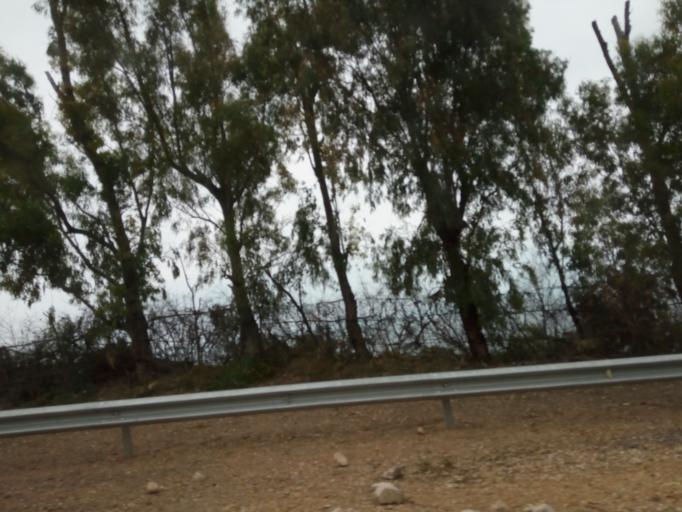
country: DZ
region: Tipaza
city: Tipasa
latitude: 36.5887
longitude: 2.5531
